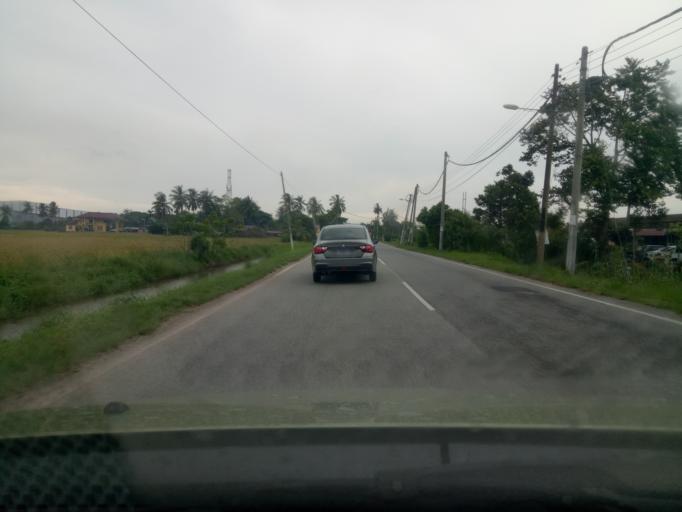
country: MY
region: Kedah
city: Alor Setar
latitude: 5.9737
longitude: 100.4067
